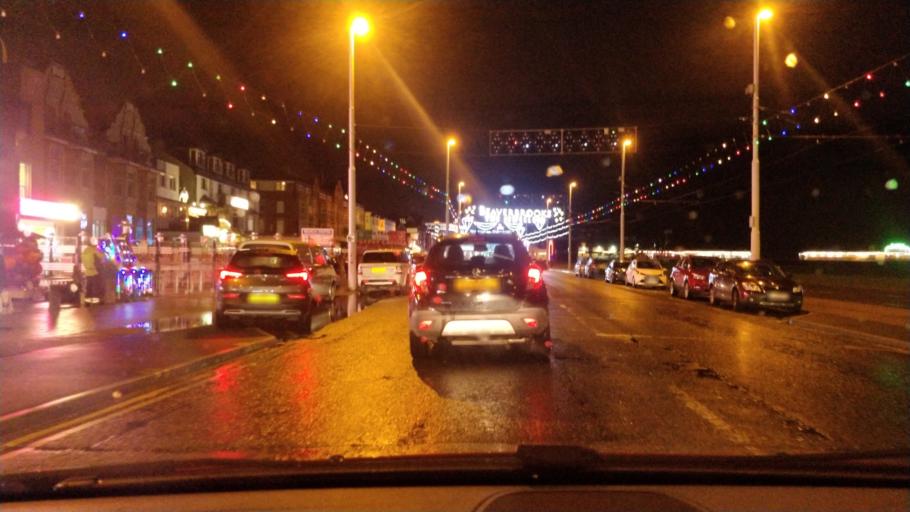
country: GB
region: England
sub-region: Blackpool
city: Blackpool
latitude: 53.7985
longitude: -3.0557
